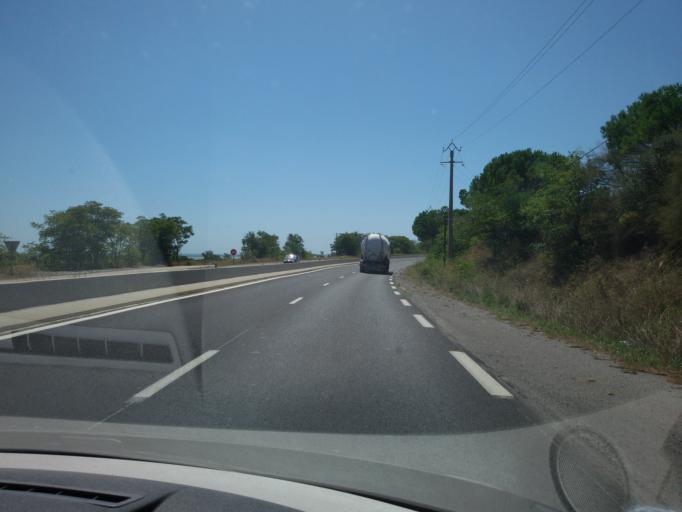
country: FR
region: Languedoc-Roussillon
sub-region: Departement de l'Herault
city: Mireval
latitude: 43.5307
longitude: 3.8226
